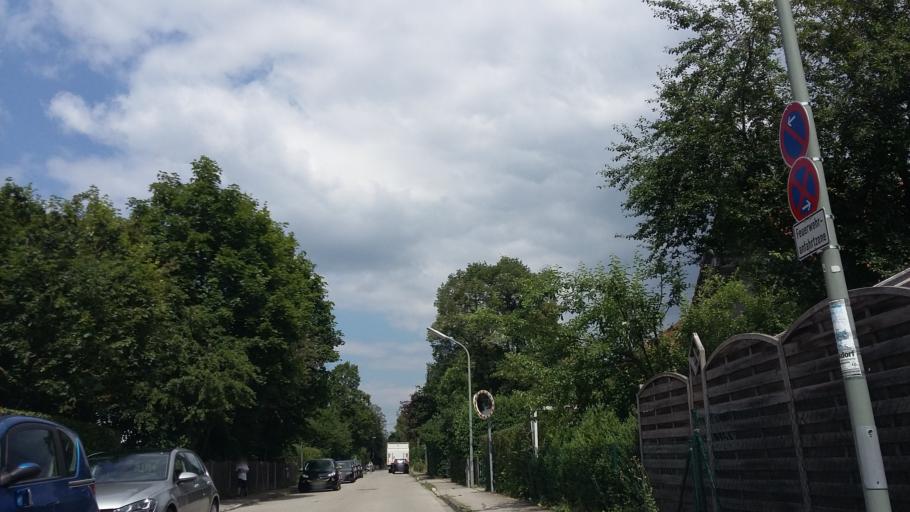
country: DE
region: Bavaria
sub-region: Upper Bavaria
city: Planegg
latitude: 48.0888
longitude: 11.4091
